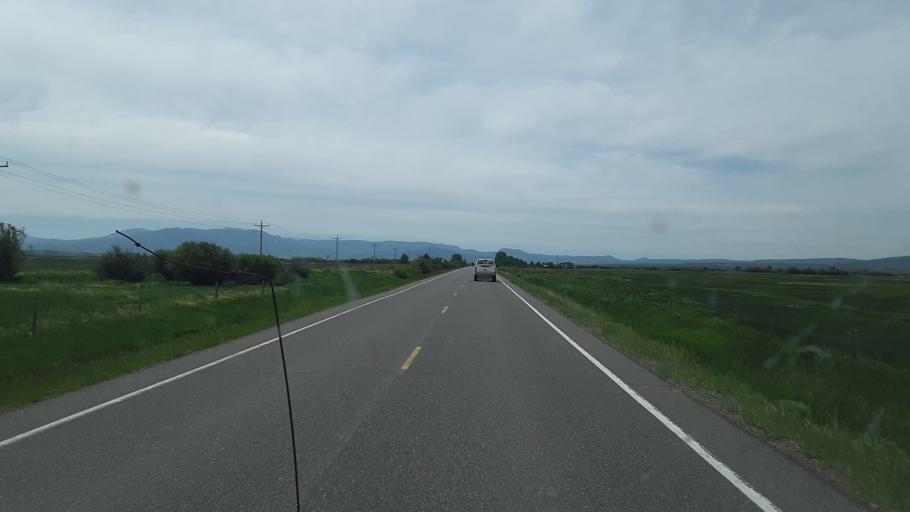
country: US
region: Colorado
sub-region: Jackson County
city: Walden
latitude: 40.6024
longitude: -106.4069
